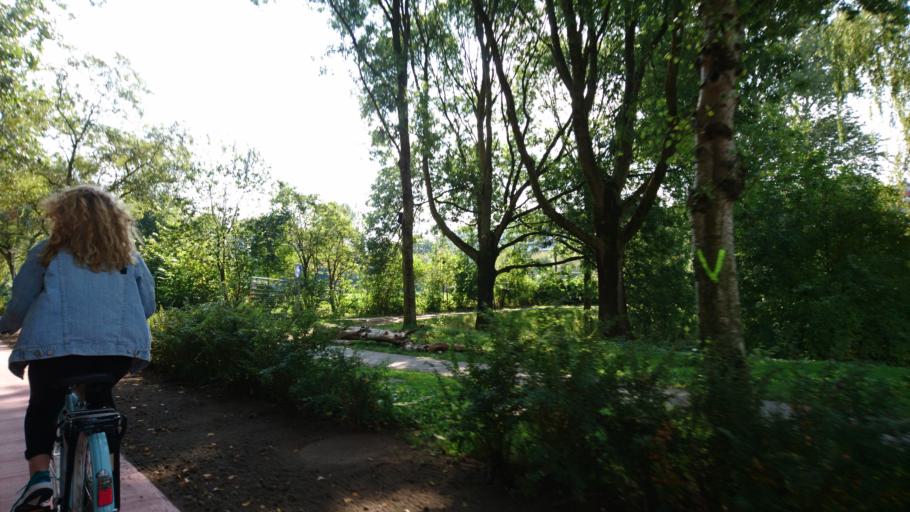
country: NL
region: Groningen
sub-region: Gemeente Groningen
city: Korrewegwijk
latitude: 53.2334
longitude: 6.5462
